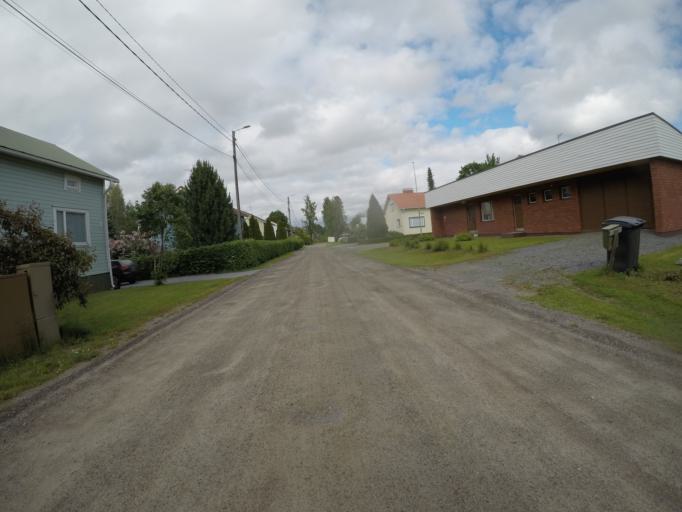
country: FI
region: Haeme
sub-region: Haemeenlinna
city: Haemeenlinna
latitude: 60.9872
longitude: 24.4338
